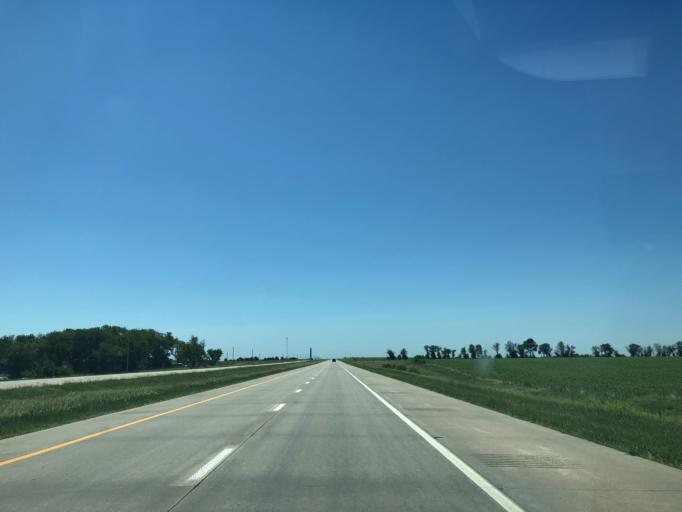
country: US
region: Kansas
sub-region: Republic County
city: Belleville
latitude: 39.9252
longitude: -97.6145
